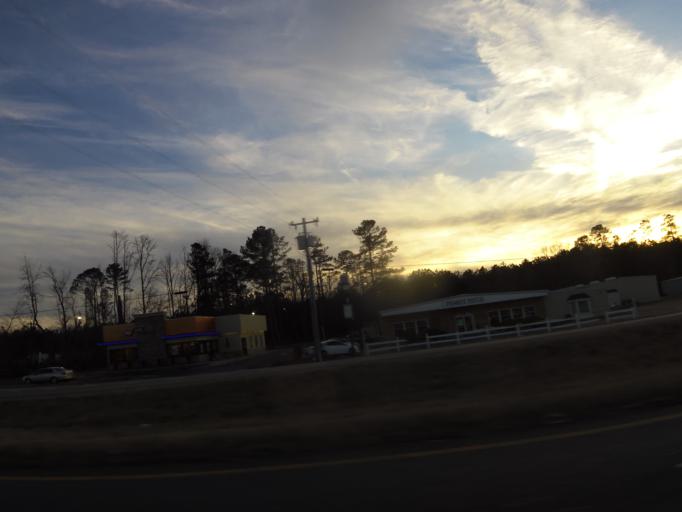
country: US
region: Virginia
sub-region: Southampton County
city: Courtland
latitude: 36.6946
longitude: -77.0343
